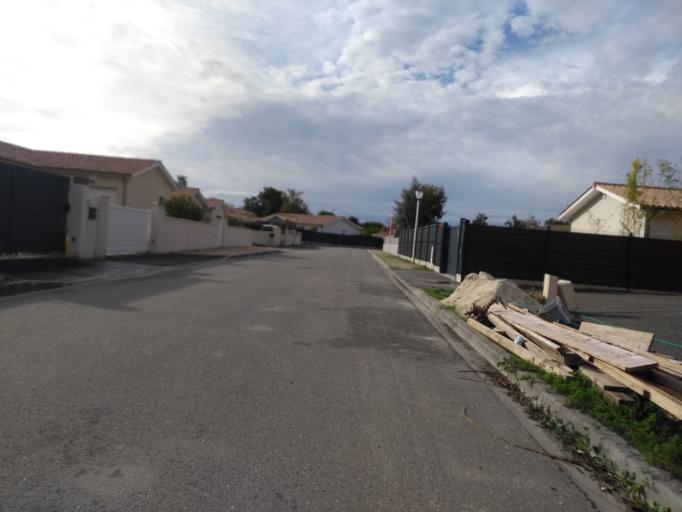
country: FR
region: Aquitaine
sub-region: Departement de la Gironde
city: Cestas
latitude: 44.7383
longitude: -0.6711
